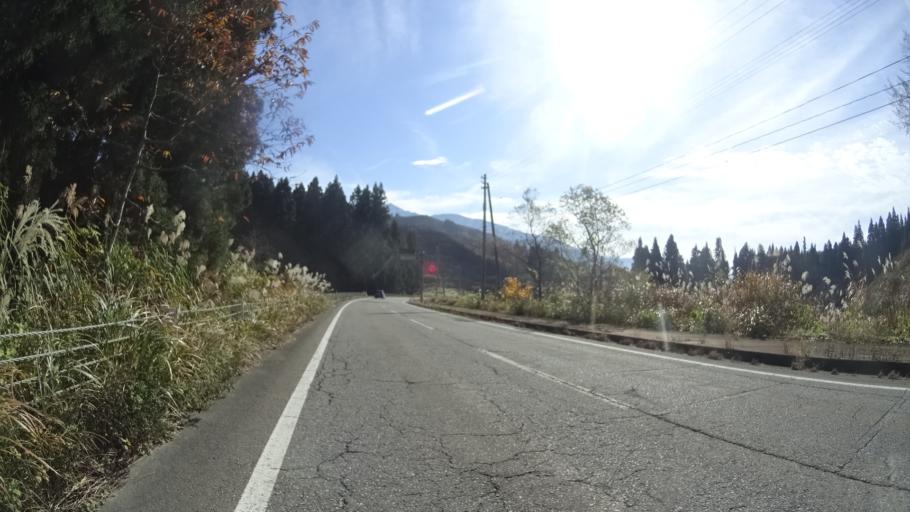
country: JP
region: Niigata
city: Muikamachi
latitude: 37.1905
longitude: 138.9811
